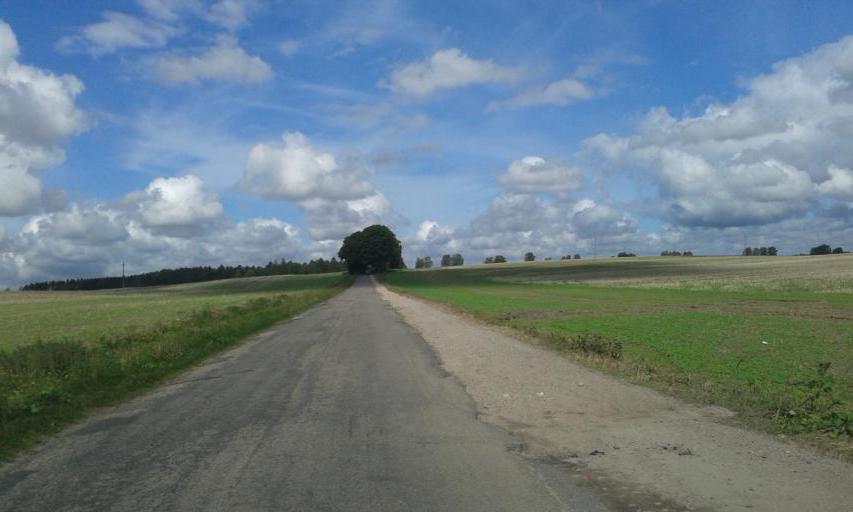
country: PL
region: West Pomeranian Voivodeship
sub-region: Powiat slawienski
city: Slawno
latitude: 54.2896
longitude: 16.6545
